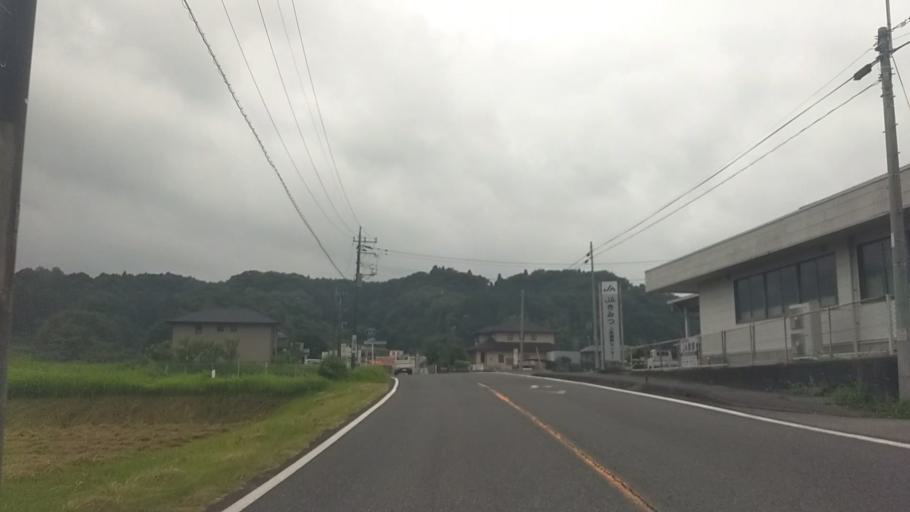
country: JP
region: Chiba
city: Kisarazu
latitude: 35.2881
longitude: 140.0832
